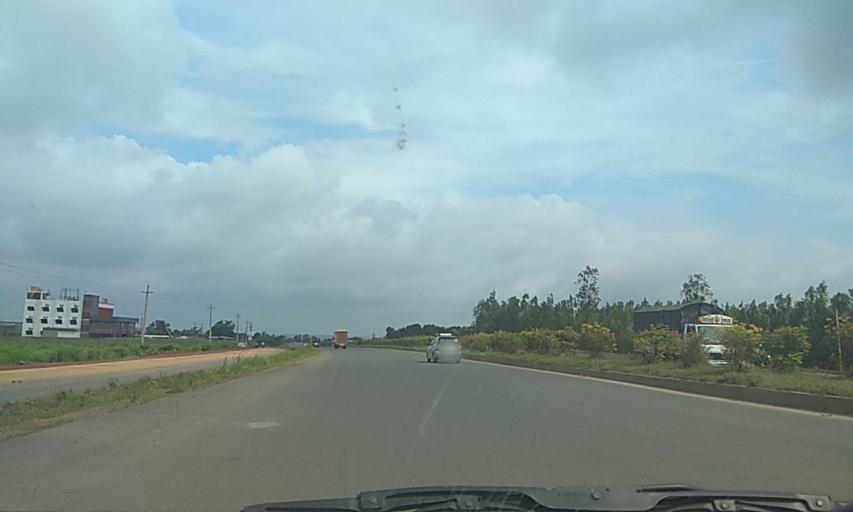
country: IN
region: Karnataka
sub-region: Dharwad
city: Kundgol
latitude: 15.1850
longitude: 75.1367
